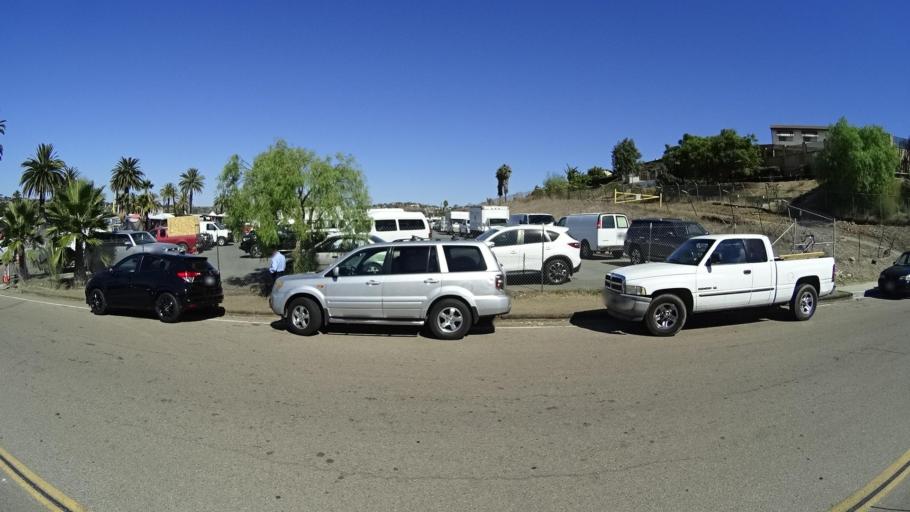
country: US
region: California
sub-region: San Diego County
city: La Presa
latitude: 32.7011
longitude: -117.0066
